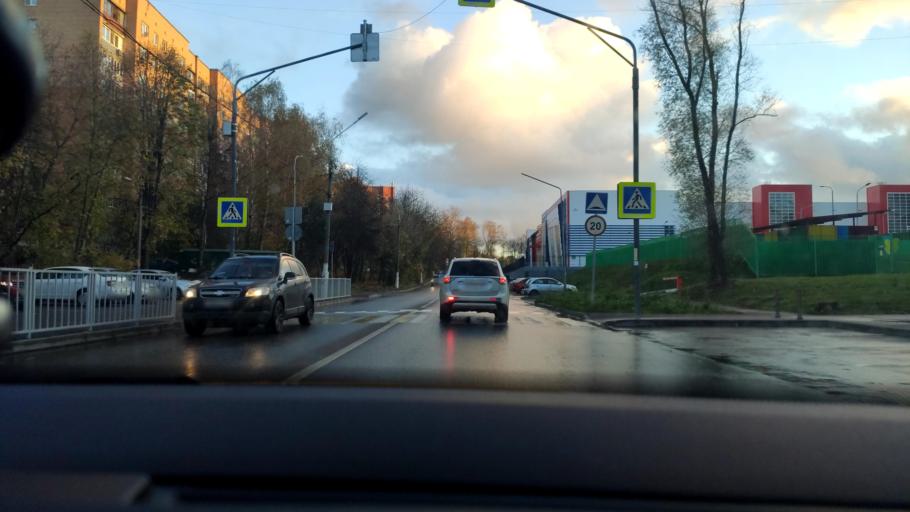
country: RU
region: Moskovskaya
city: Krasnogorsk
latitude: 55.8323
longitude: 37.3249
